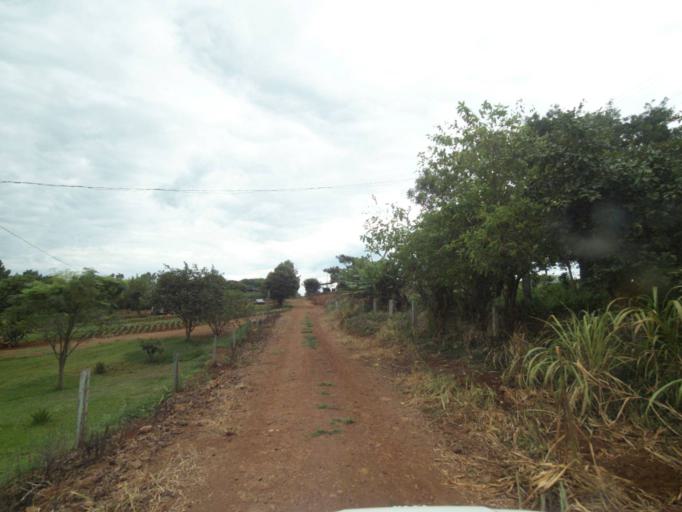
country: BR
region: Parana
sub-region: Guaraniacu
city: Guaraniacu
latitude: -24.9086
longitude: -52.9363
